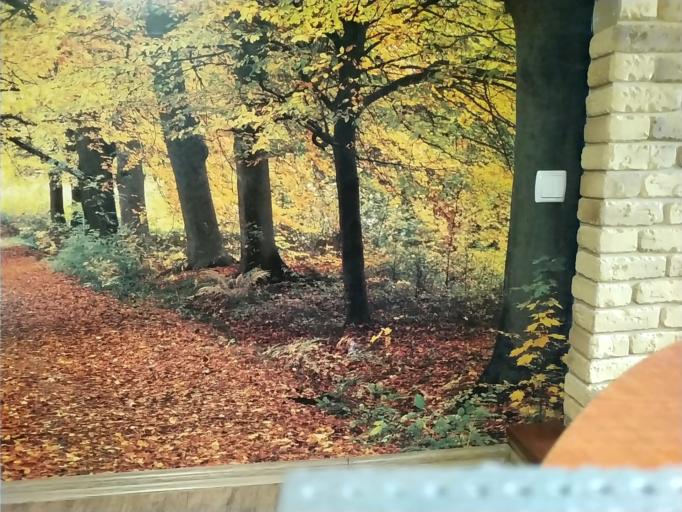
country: RU
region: Tverskaya
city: Kalashnikovo
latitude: 57.2661
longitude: 35.1545
